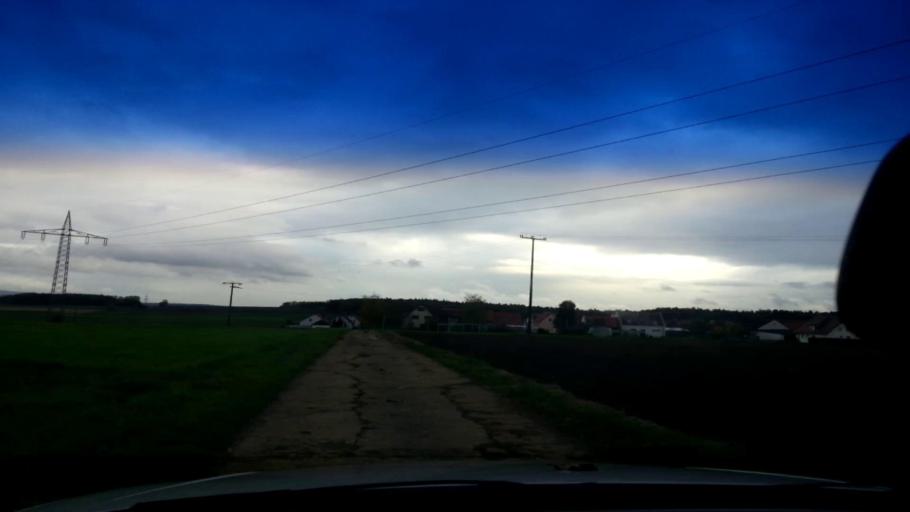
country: DE
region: Bavaria
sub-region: Upper Franconia
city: Gundelsheim
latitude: 49.9616
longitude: 10.9430
